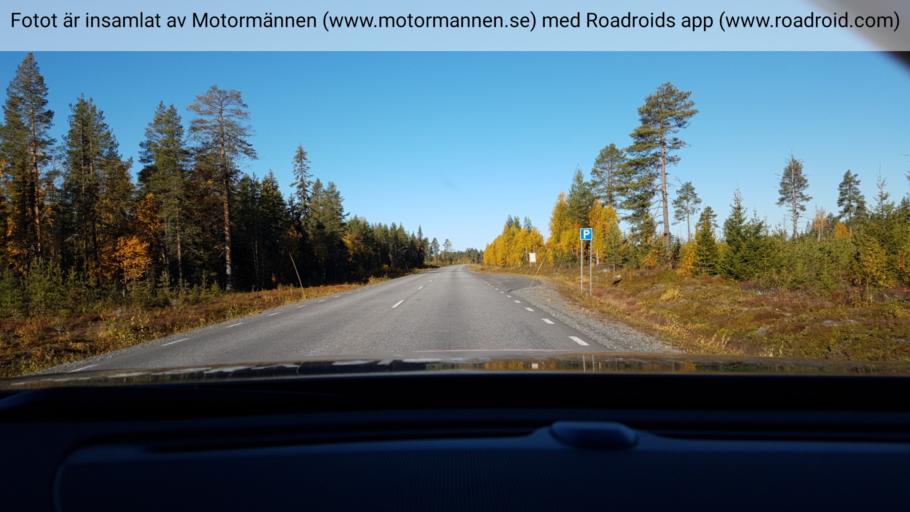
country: SE
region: Vaesterbotten
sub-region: Skelleftea Kommun
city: Storvik
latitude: 65.3738
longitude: 20.3765
